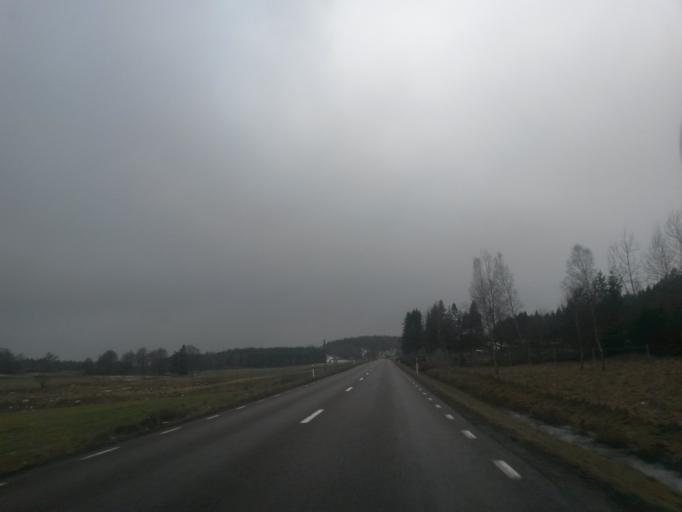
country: SE
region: Vaestra Goetaland
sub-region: Alingsas Kommun
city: Sollebrunn
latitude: 58.1371
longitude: 12.4374
